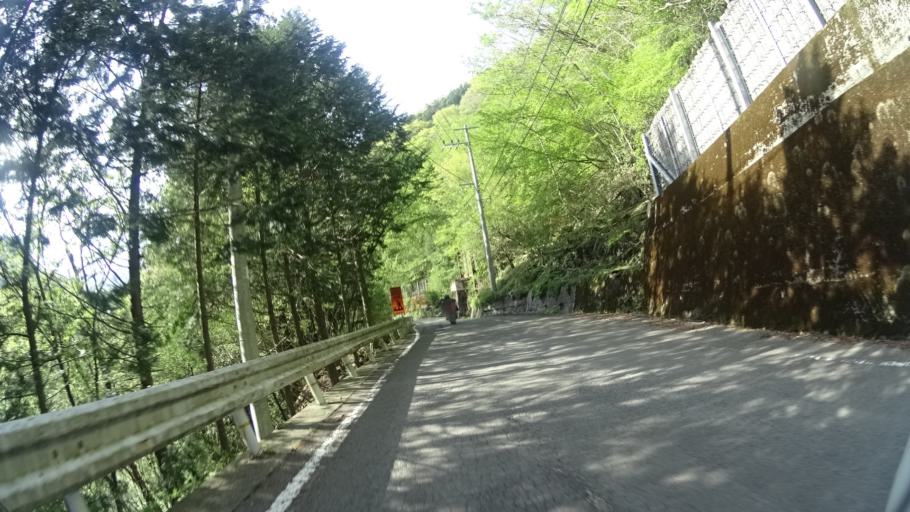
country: JP
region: Tokushima
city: Wakimachi
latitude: 33.8653
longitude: 134.0078
